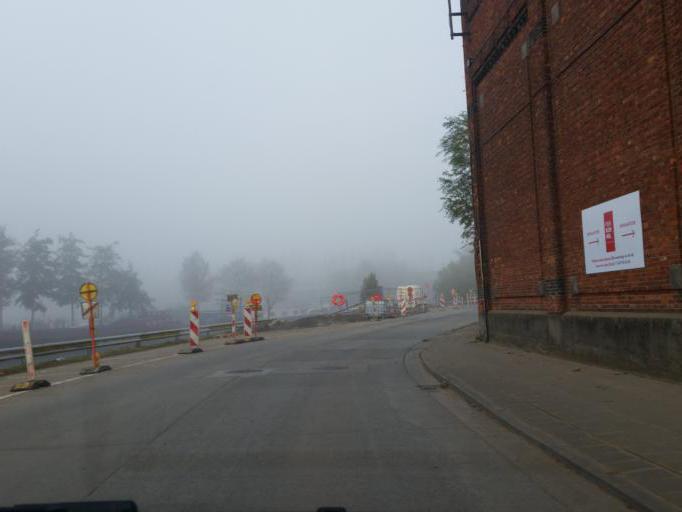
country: BE
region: Flanders
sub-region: Provincie Oost-Vlaanderen
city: Aalst
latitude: 50.9476
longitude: 4.0376
